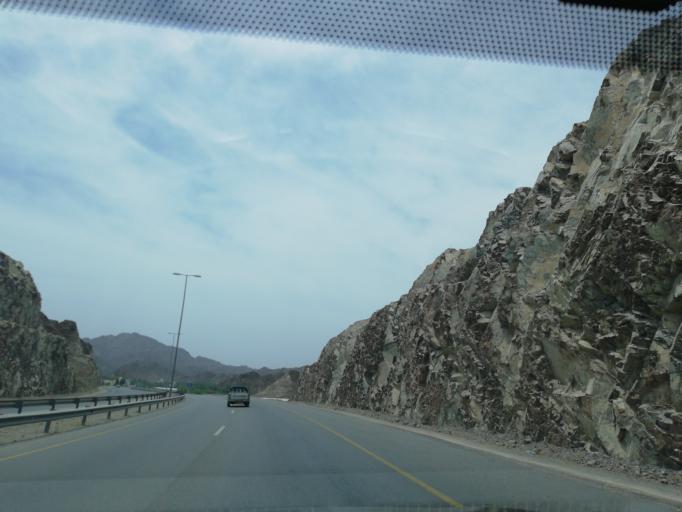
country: OM
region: Muhafazat ad Dakhiliyah
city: Sufalat Sama'il
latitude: 23.3622
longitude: 58.0325
